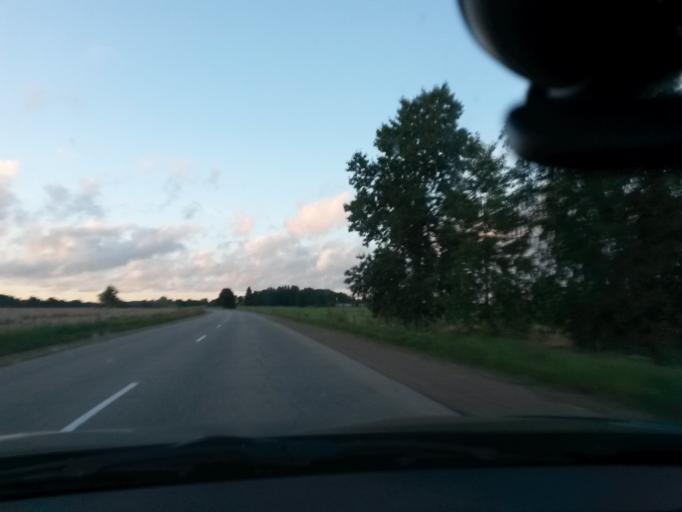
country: LV
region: Madonas Rajons
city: Madona
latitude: 56.7384
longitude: 26.0180
